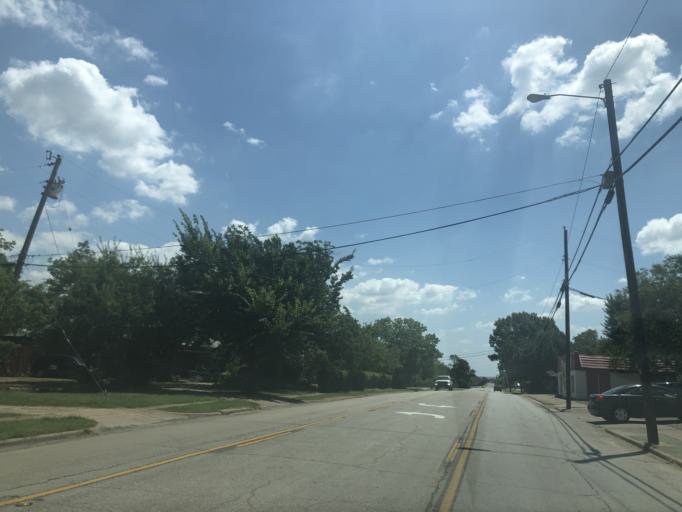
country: US
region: Texas
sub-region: Dallas County
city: Grand Prairie
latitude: 32.7446
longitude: -97.0262
